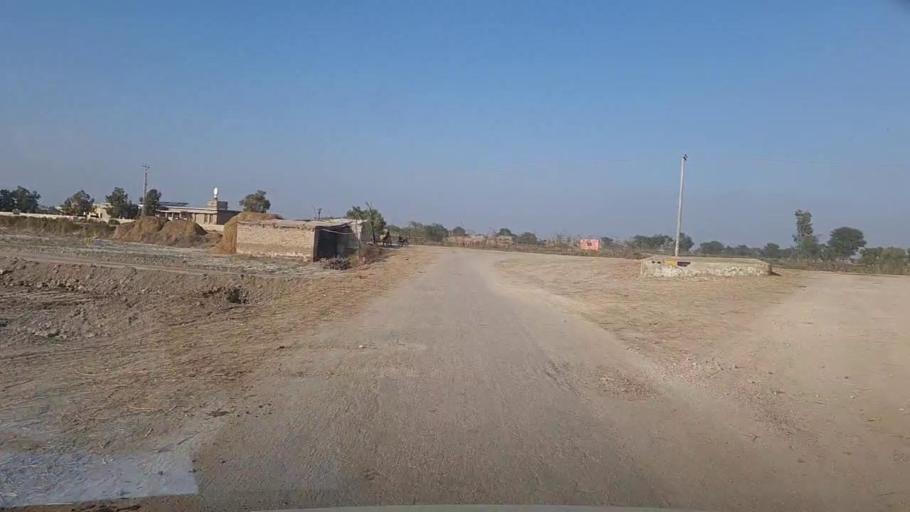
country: PK
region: Sindh
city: Phulji
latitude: 26.8571
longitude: 67.7937
